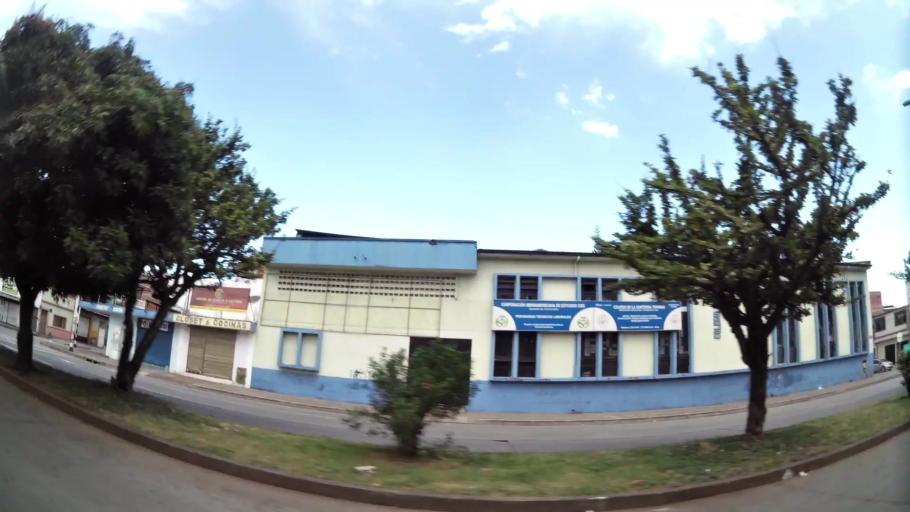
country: CO
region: Valle del Cauca
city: Cali
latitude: 3.4410
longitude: -76.5258
